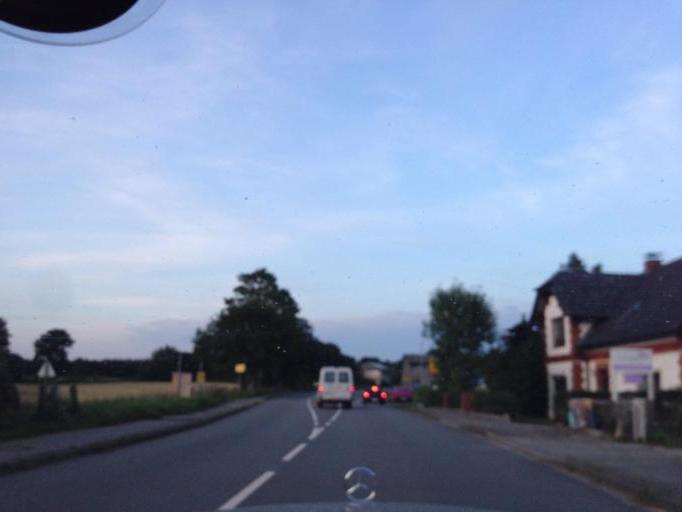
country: DE
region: Schleswig-Holstein
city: Hammoor
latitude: 53.7139
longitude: 10.3259
